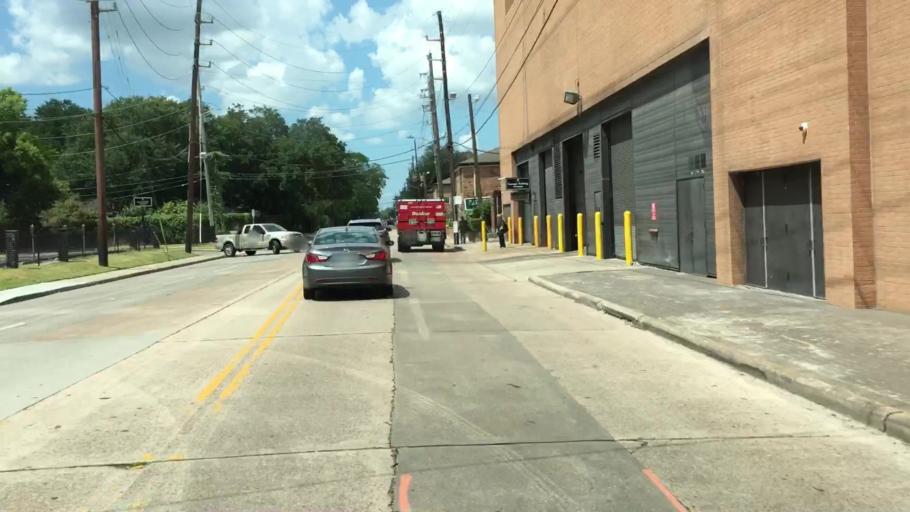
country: US
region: Texas
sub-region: Harris County
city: Bellaire
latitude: 29.7411
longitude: -95.4669
